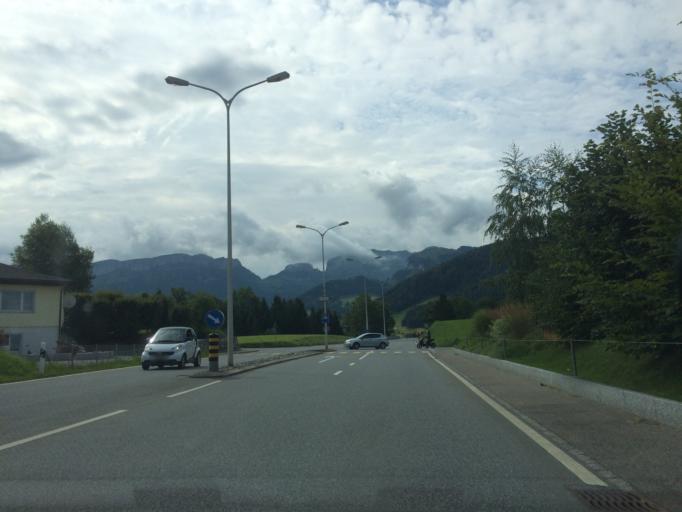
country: CH
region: Appenzell Innerrhoden
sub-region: Appenzell Inner Rhodes
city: Appenzell
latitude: 47.3283
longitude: 9.4269
